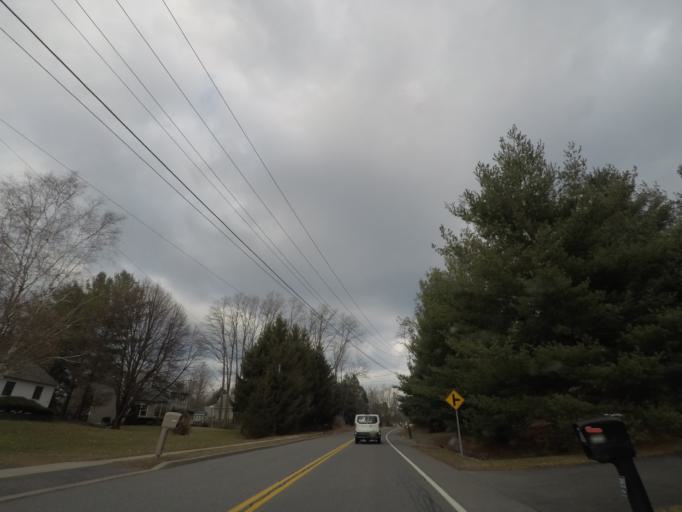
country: US
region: New York
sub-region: Albany County
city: Westmere
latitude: 42.6738
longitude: -73.8759
